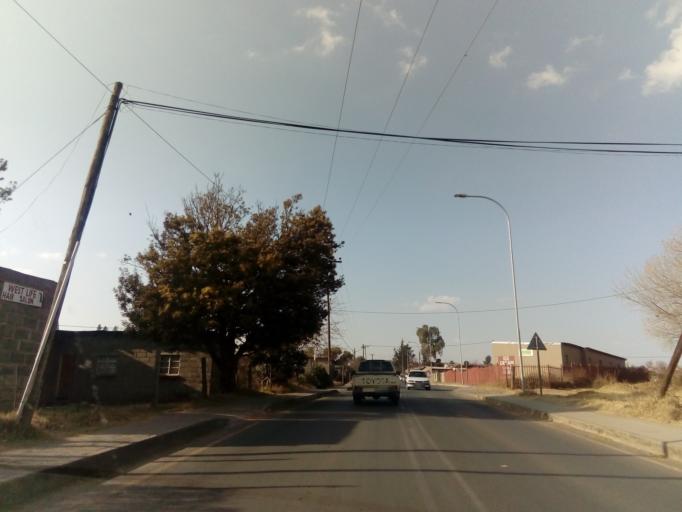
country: LS
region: Maseru
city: Maseru
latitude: -29.3071
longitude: 27.5313
